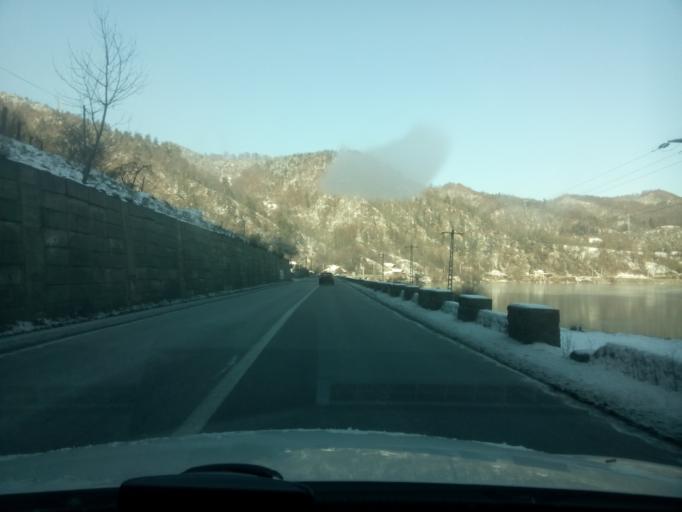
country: RO
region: Valcea
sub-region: Comuna Brezoi
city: Brezoi
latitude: 45.3504
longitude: 24.2622
